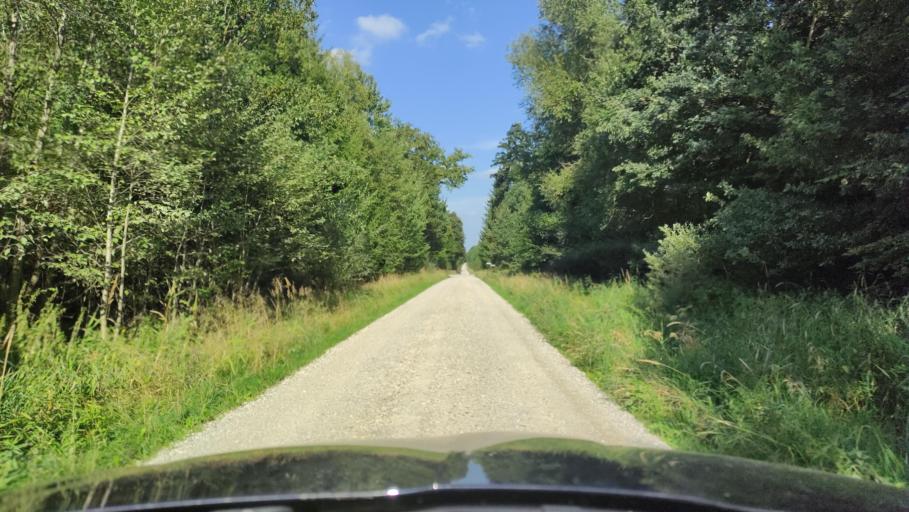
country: DE
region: Bavaria
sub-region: Swabia
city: Roggenburg
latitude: 48.2806
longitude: 10.2762
